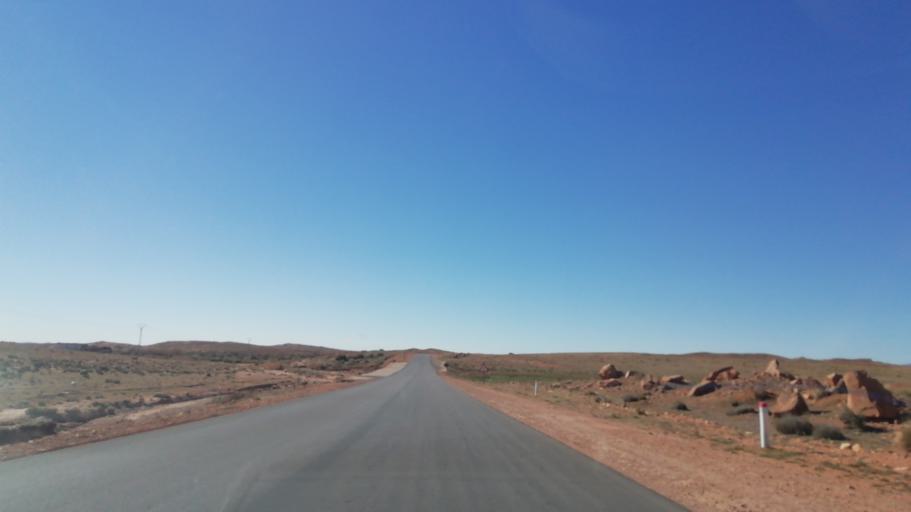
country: DZ
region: El Bayadh
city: El Bayadh
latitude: 33.6440
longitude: 1.3928
